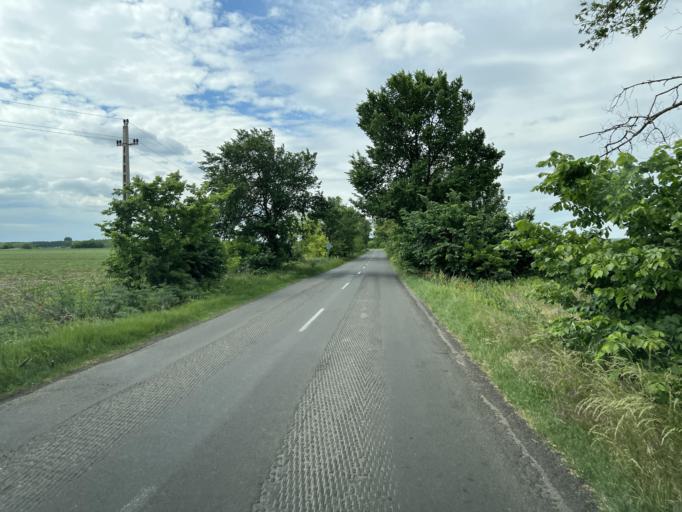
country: HU
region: Pest
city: Szentmartonkata
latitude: 47.4822
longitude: 19.7272
